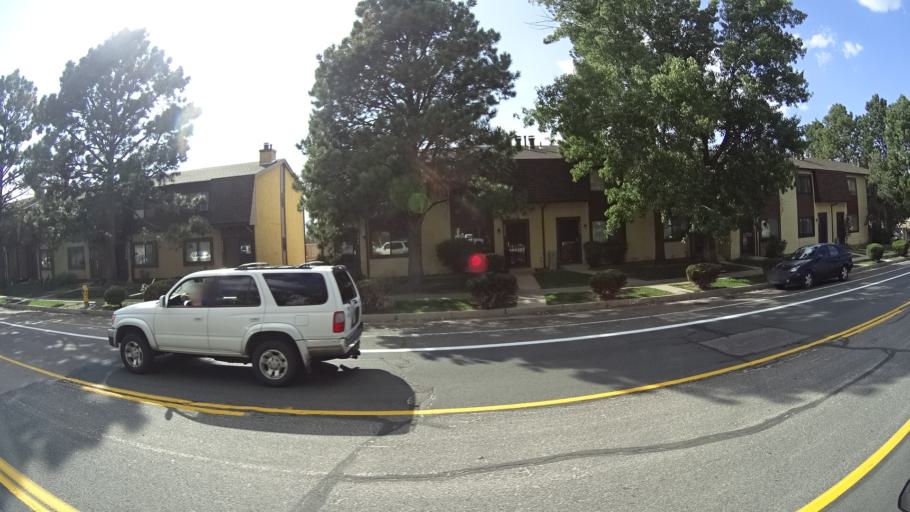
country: US
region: Colorado
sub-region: El Paso County
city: Cimarron Hills
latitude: 38.8875
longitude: -104.7386
